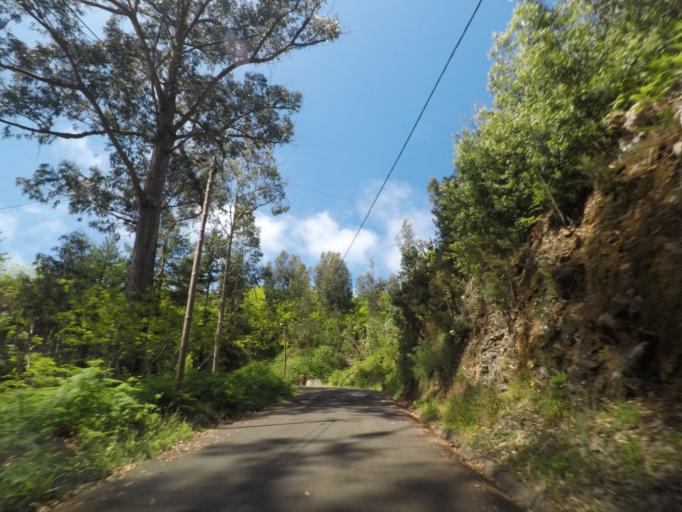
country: PT
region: Madeira
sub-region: Calheta
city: Arco da Calheta
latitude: 32.7277
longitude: -17.1331
